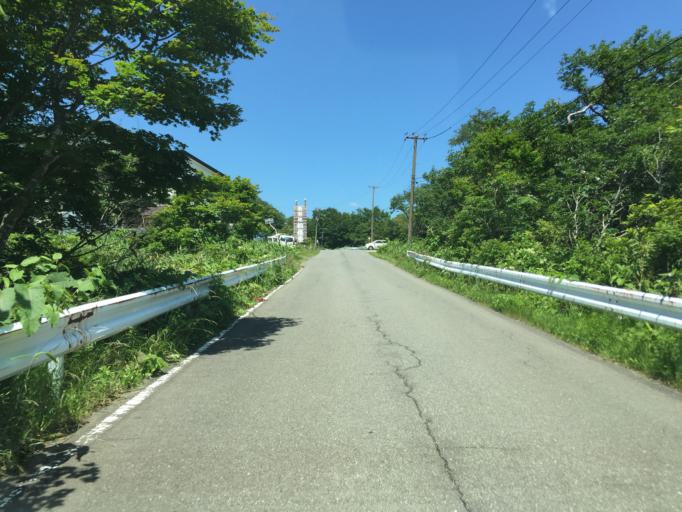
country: JP
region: Fukushima
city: Inawashiro
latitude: 37.6695
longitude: 140.2680
